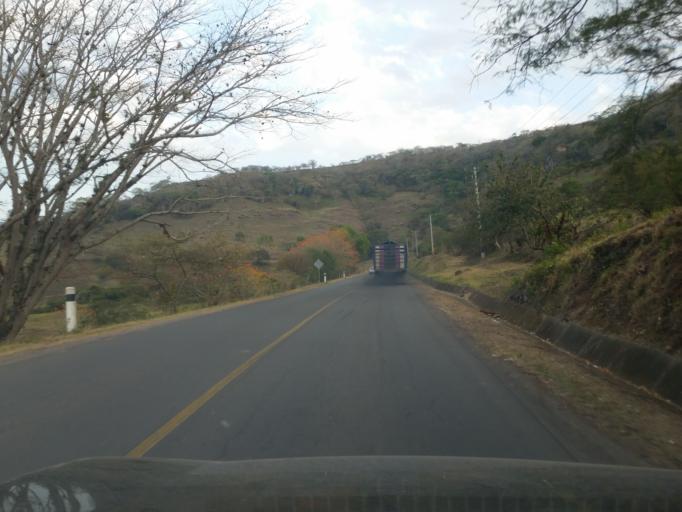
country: NI
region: Jinotega
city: Jinotega
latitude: 13.1340
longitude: -86.0192
